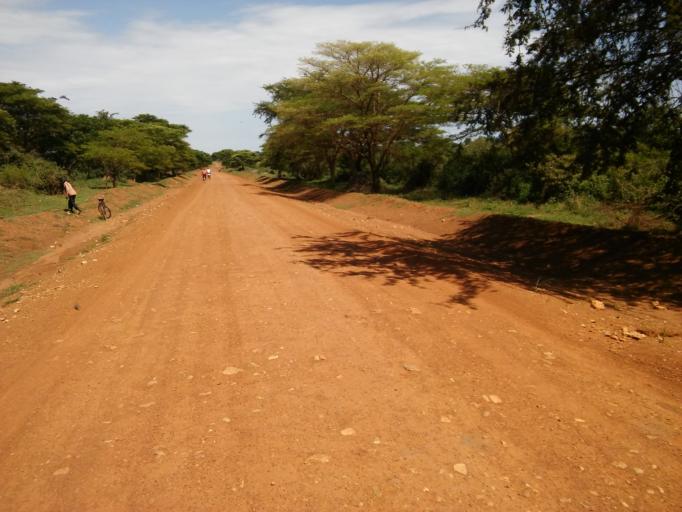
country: UG
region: Eastern Region
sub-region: Kumi District
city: Kumi
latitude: 1.4847
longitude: 33.9149
